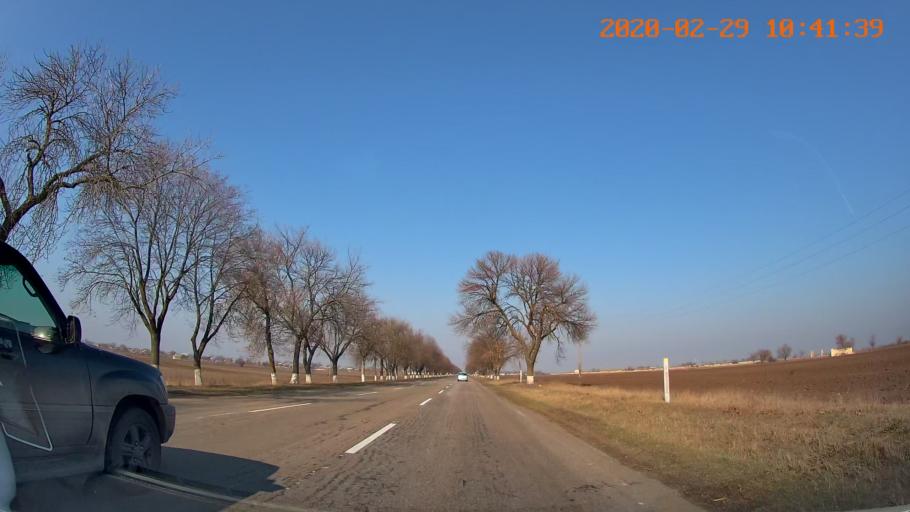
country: MD
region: Telenesti
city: Grigoriopol
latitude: 47.0444
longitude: 29.4221
